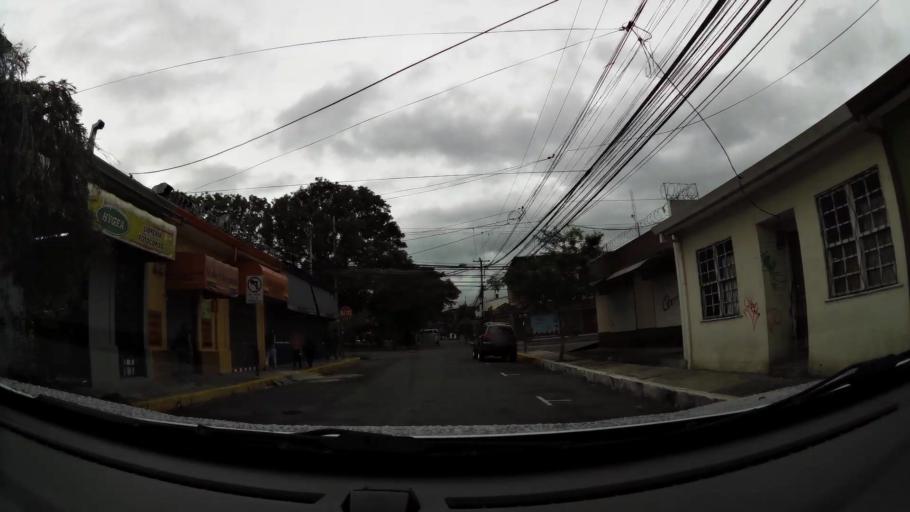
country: CR
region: San Jose
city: San Jose
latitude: 9.9350
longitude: -84.0962
